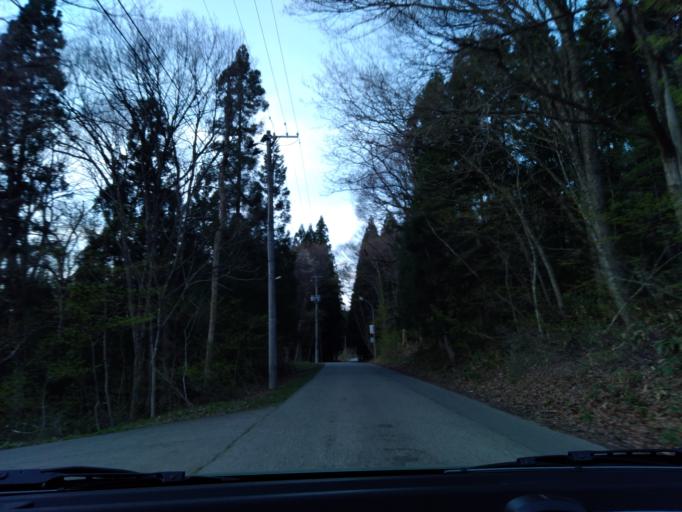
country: JP
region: Akita
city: Kakunodatemachi
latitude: 39.5889
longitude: 140.5770
